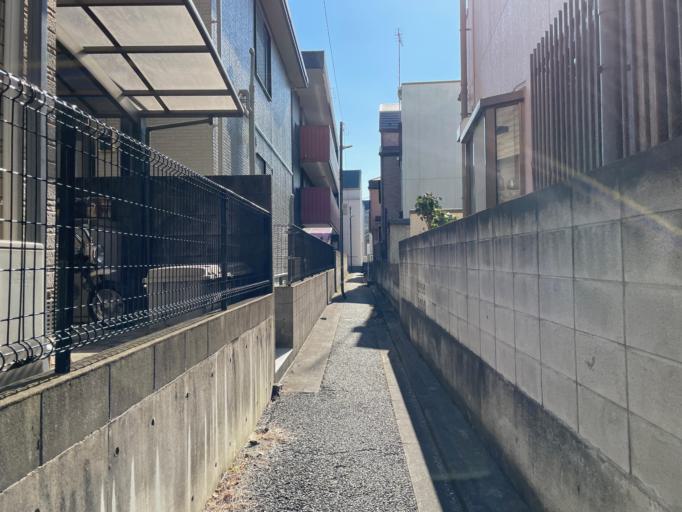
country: JP
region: Saitama
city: Soka
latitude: 35.7819
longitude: 139.7815
